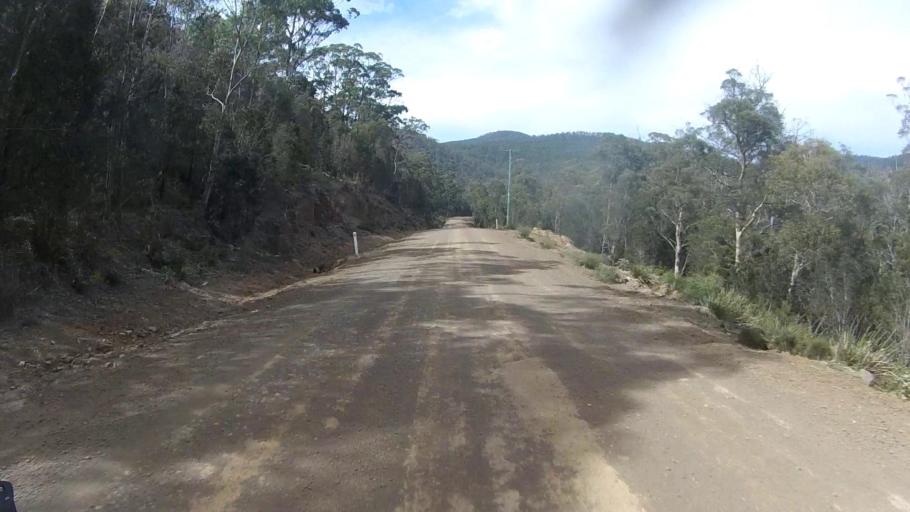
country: AU
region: Tasmania
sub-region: Sorell
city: Sorell
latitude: -42.6744
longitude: 147.8835
